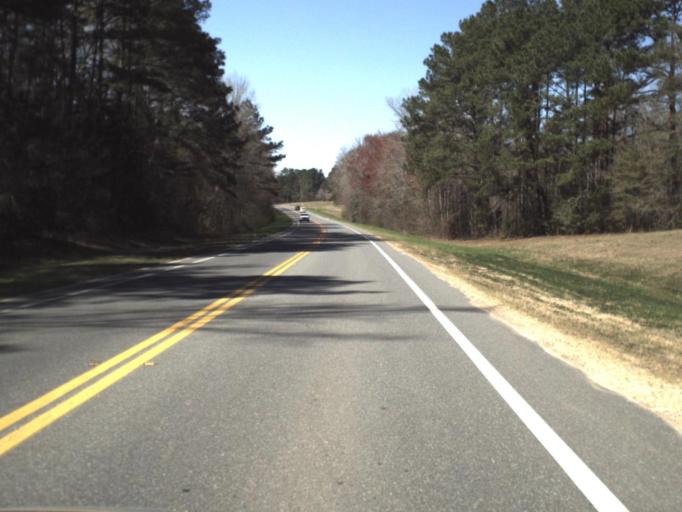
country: US
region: Florida
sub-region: Jackson County
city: Marianna
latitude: 30.7404
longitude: -85.1239
